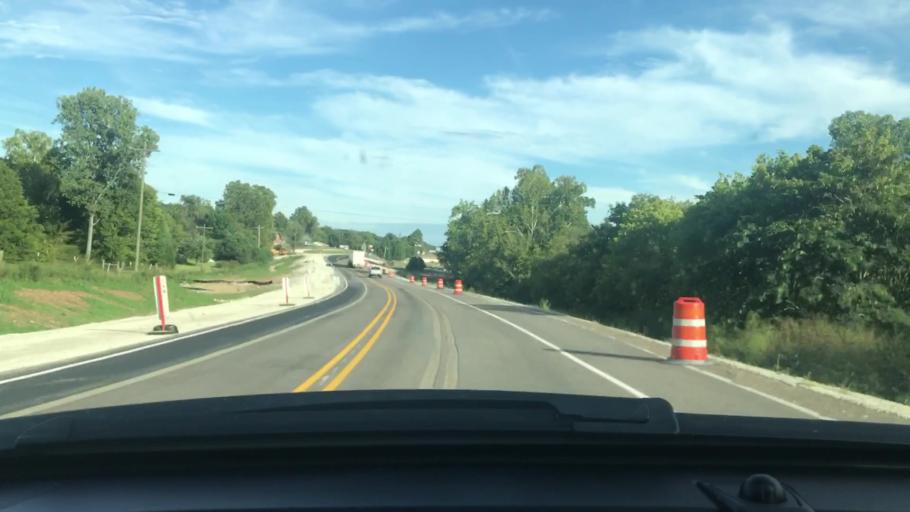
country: US
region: Arkansas
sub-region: Sharp County
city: Cherokee Village
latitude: 36.3043
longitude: -91.4495
